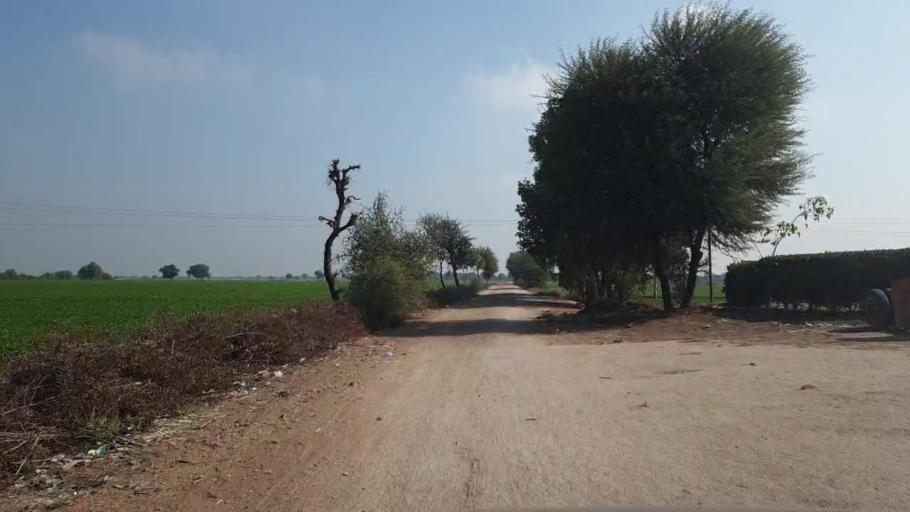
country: PK
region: Sindh
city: Shahdadpur
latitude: 26.0237
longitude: 68.5946
